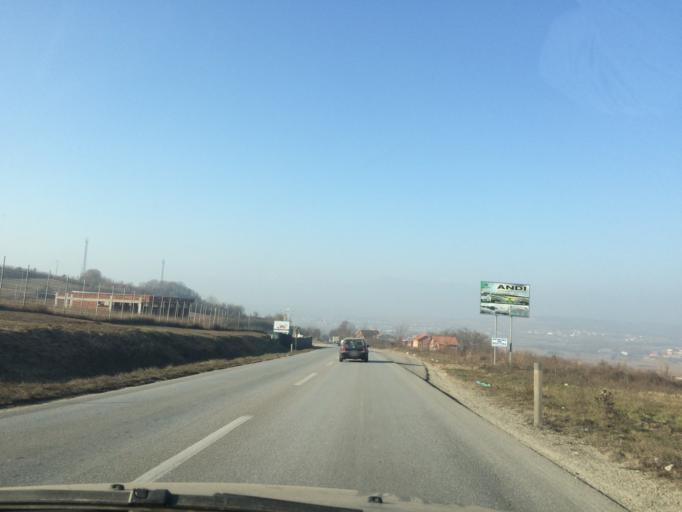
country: XK
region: Pec
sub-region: Komuna e Klines
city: Klina
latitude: 42.5933
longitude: 20.5995
